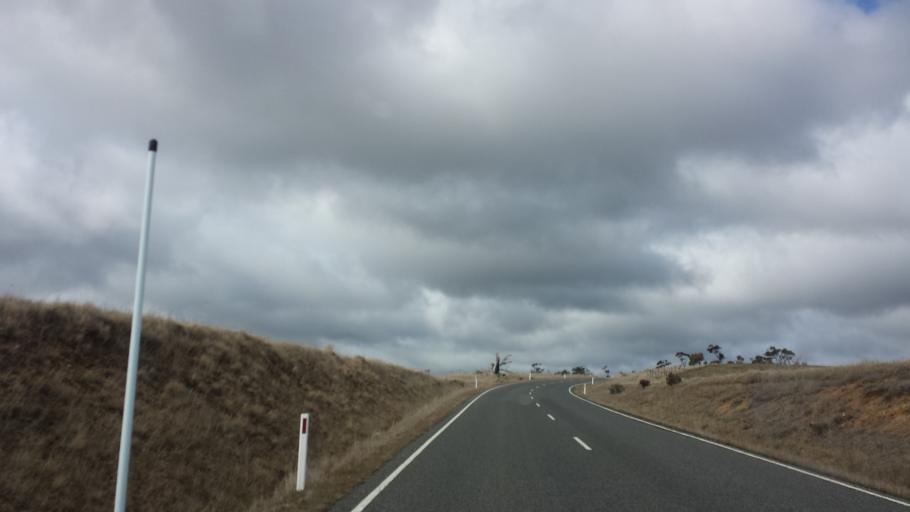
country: AU
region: Victoria
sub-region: Alpine
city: Mount Beauty
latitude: -37.1156
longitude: 147.4372
